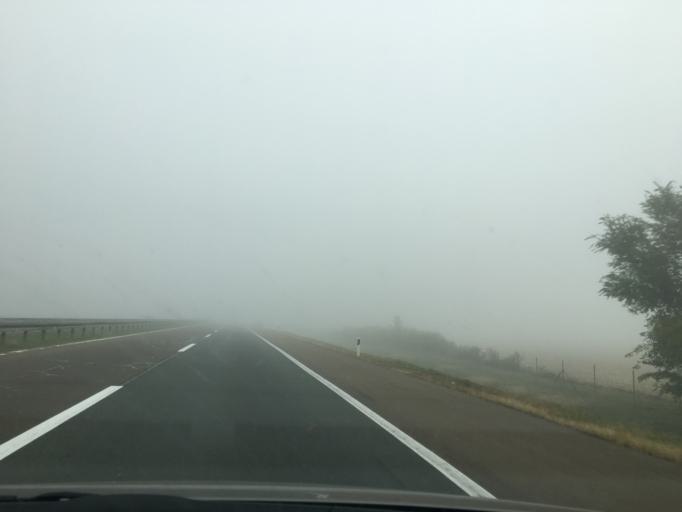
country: RS
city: Novi Karlovci
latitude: 45.0335
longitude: 20.1862
